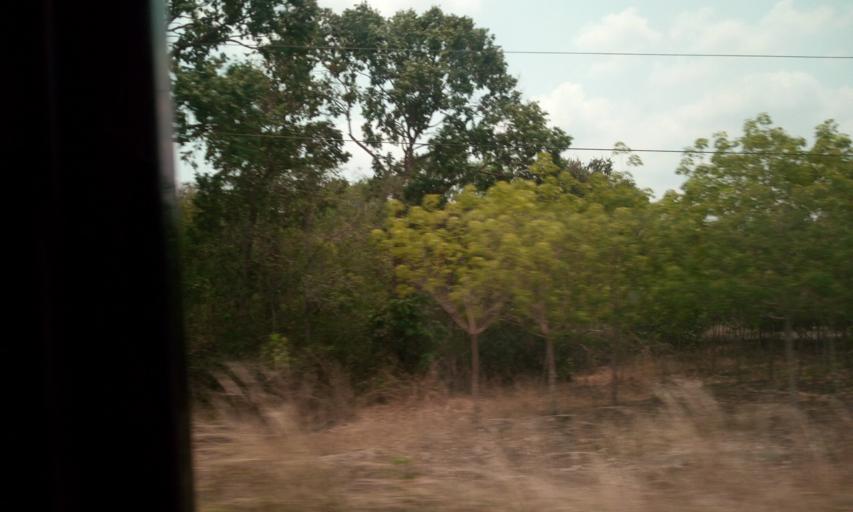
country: TH
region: Phayao
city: Phu Sang
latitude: 19.6097
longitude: 100.2987
